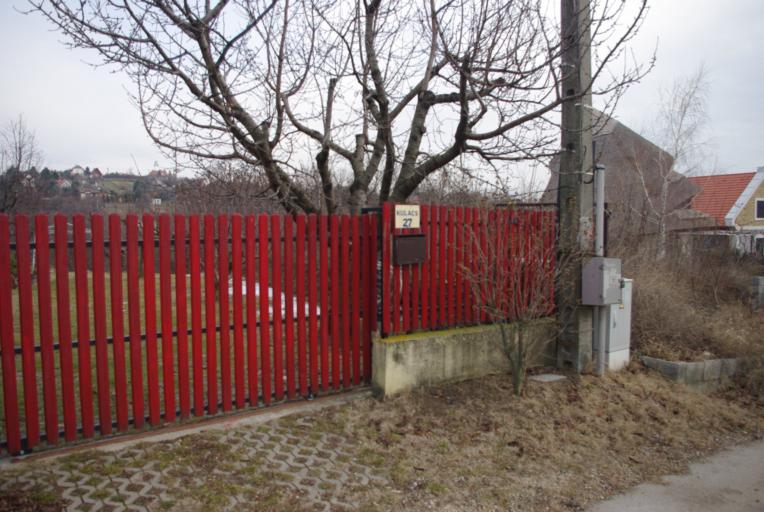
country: HU
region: Fejer
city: Gardony
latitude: 47.2476
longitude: 18.5945
